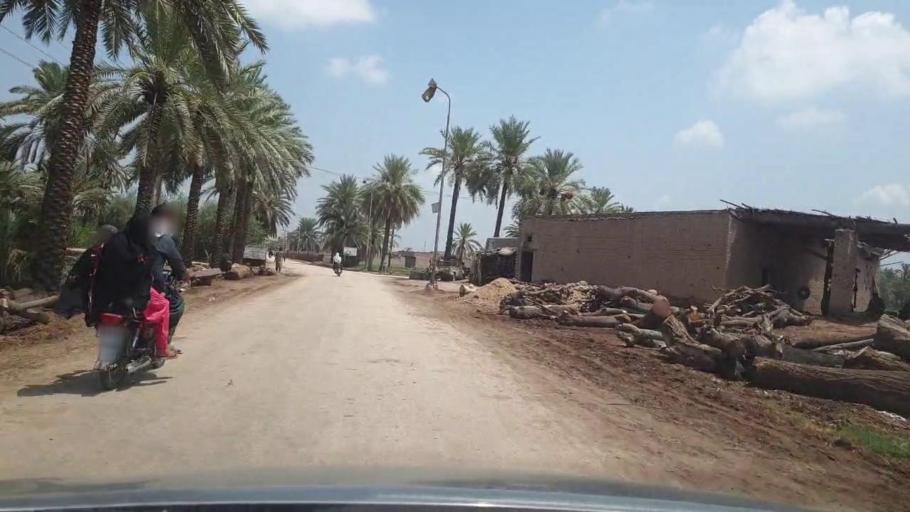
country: PK
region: Sindh
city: Pir jo Goth
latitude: 27.5962
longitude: 68.6095
